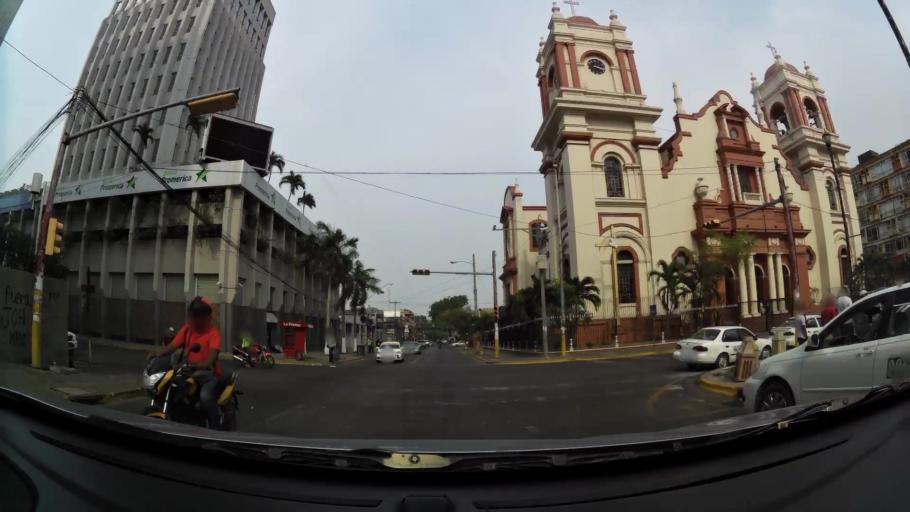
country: HN
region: Cortes
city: San Pedro Sula
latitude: 15.5057
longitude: -88.0246
